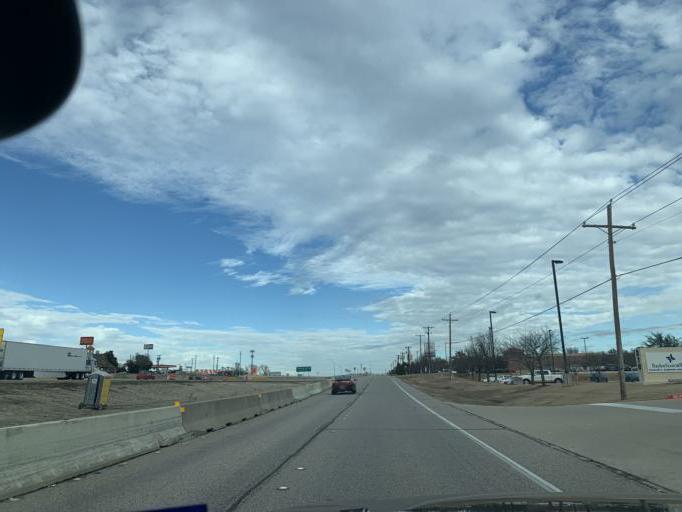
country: US
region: Texas
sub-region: Dallas County
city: Duncanville
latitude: 32.6297
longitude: -96.9028
